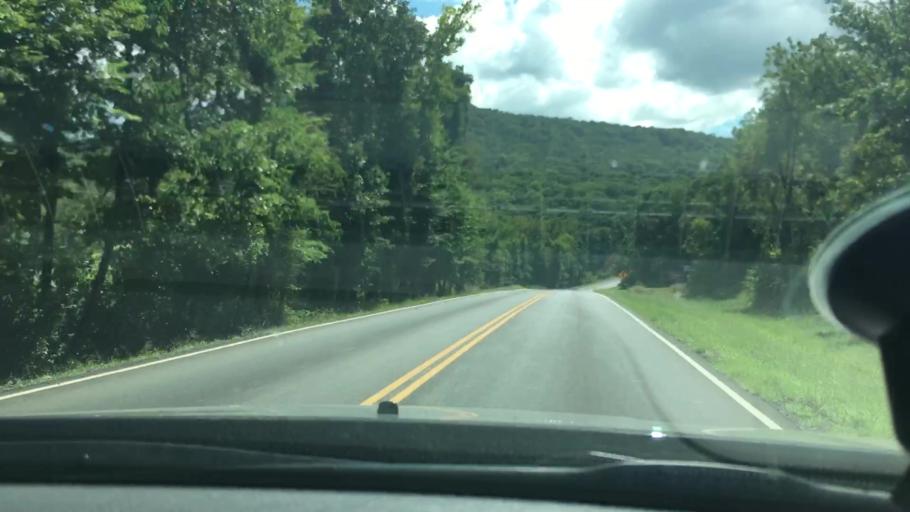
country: US
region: Oklahoma
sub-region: Sequoyah County
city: Vian
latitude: 35.6701
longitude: -94.9342
